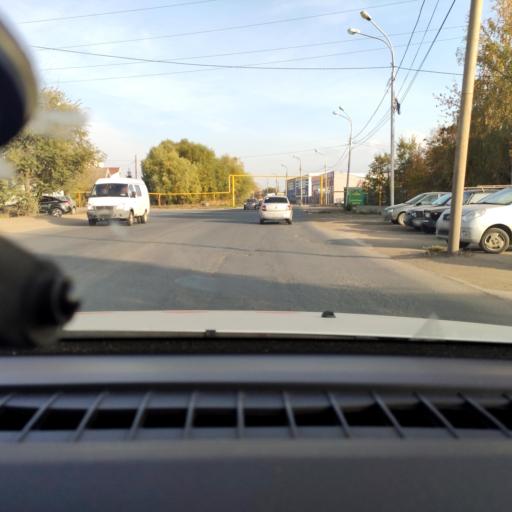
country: RU
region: Samara
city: Samara
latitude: 53.1347
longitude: 50.1152
